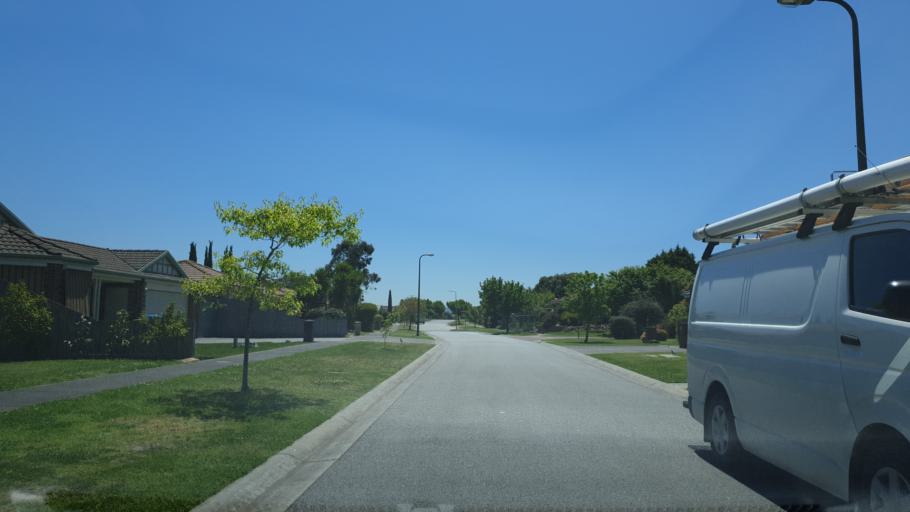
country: AU
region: Victoria
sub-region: Casey
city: Cranbourne North
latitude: -38.0835
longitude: 145.2932
